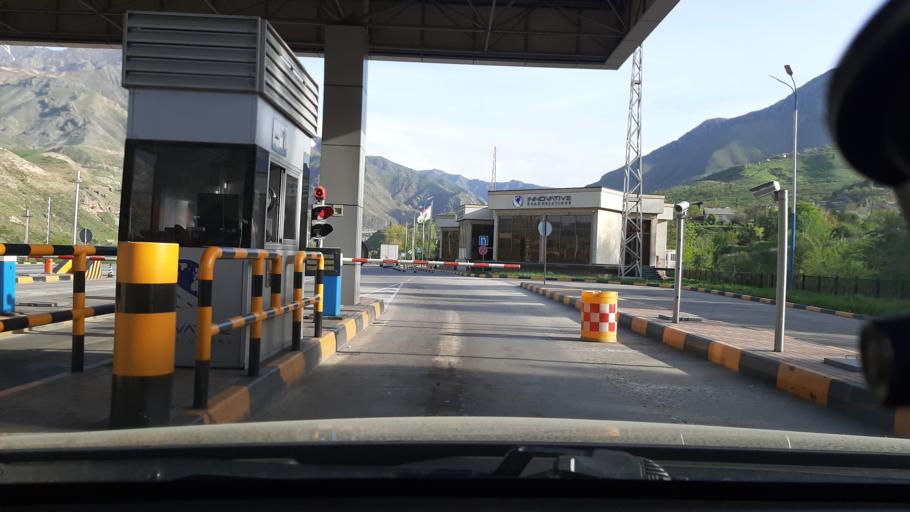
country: TJ
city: Varzob
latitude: 38.6833
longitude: 68.7916
